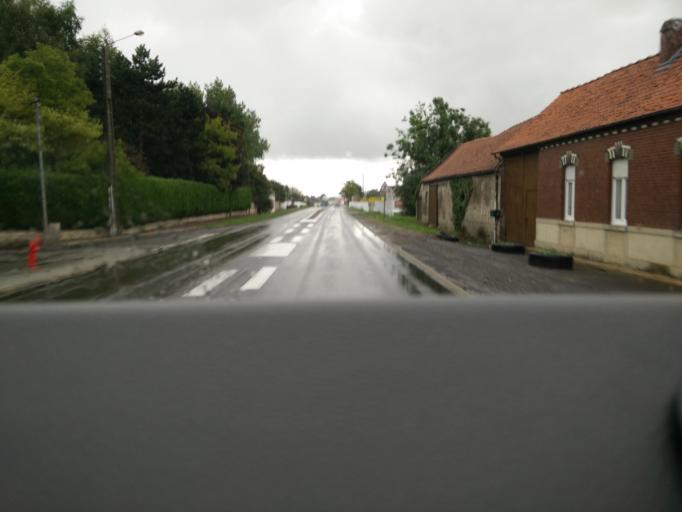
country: FR
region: Nord-Pas-de-Calais
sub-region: Departement du Pas-de-Calais
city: Savy-Berlette
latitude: 50.3554
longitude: 2.4817
